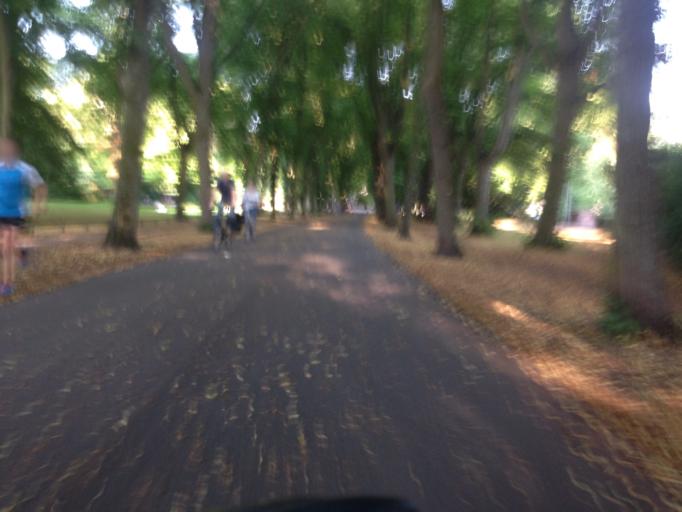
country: DE
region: North Rhine-Westphalia
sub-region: Regierungsbezirk Munster
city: Muenster
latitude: 51.9671
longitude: 7.6208
